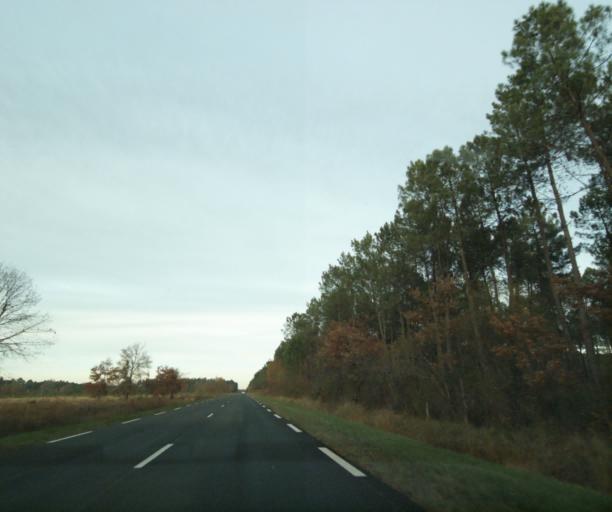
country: FR
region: Aquitaine
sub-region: Departement de la Gironde
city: Bazas
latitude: 44.3257
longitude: -0.2407
